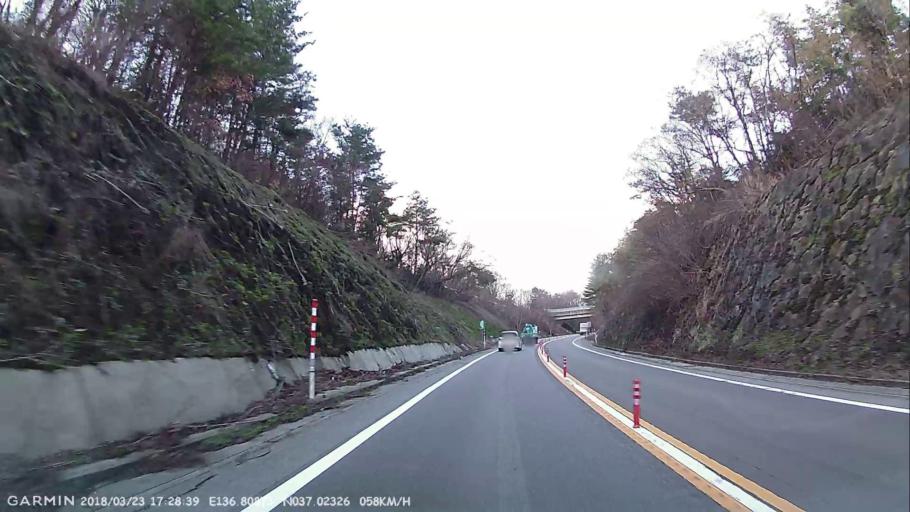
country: JP
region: Ishikawa
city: Hakui
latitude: 37.0234
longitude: 136.8088
